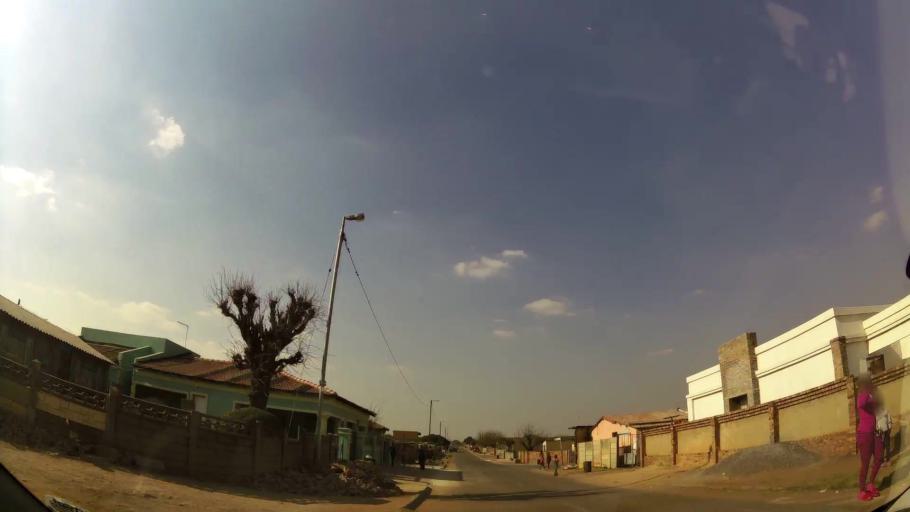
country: ZA
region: Gauteng
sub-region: Ekurhuleni Metropolitan Municipality
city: Brakpan
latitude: -26.1580
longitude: 28.4053
